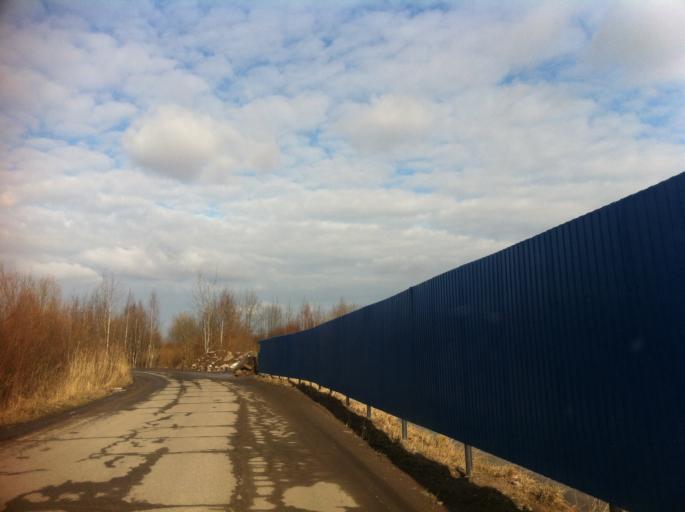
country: RU
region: Leningrad
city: Yanino Vtoroye
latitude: 59.9554
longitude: 30.5772
